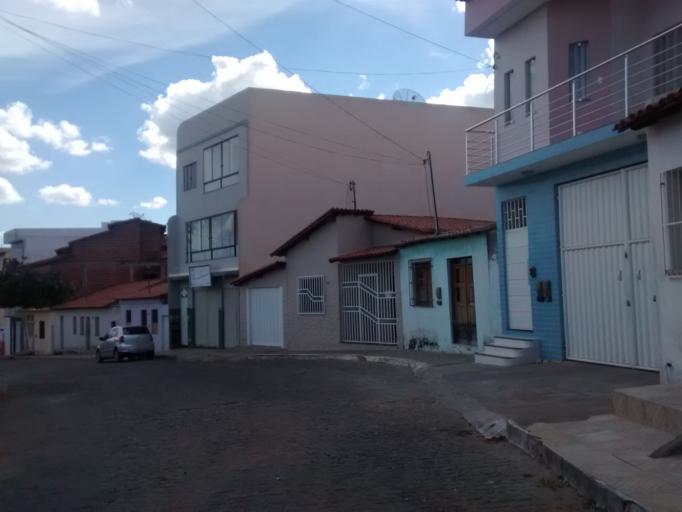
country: BR
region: Bahia
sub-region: Brumado
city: Brumado
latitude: -14.2092
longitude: -41.6761
